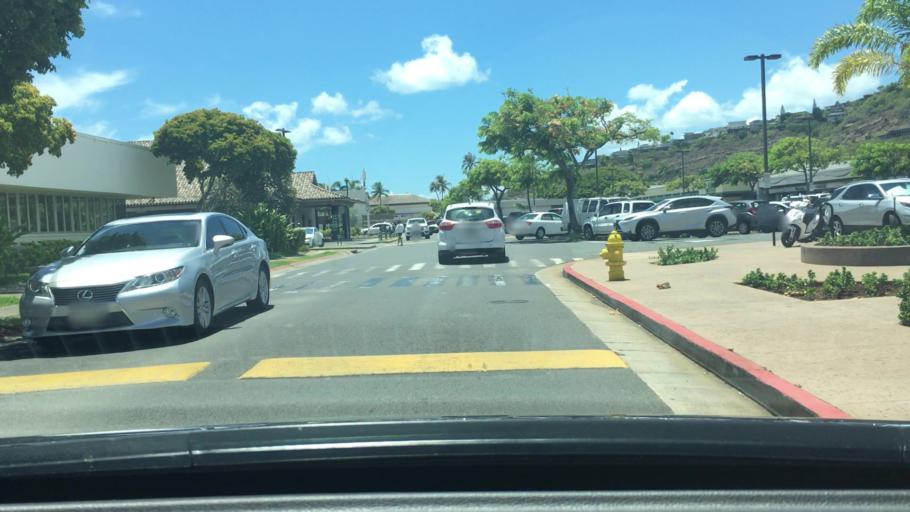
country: US
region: Hawaii
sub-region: Honolulu County
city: Waimanalo
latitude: 21.2788
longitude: -157.7530
